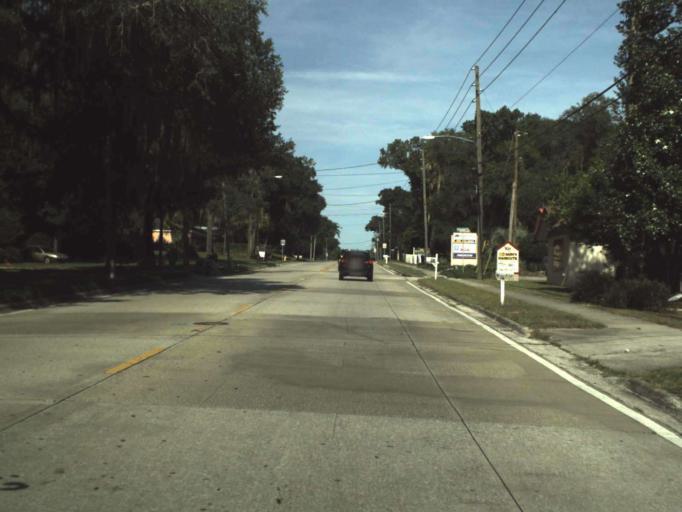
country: US
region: Florida
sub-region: Volusia County
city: DeLand
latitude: 29.0282
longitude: -81.2885
